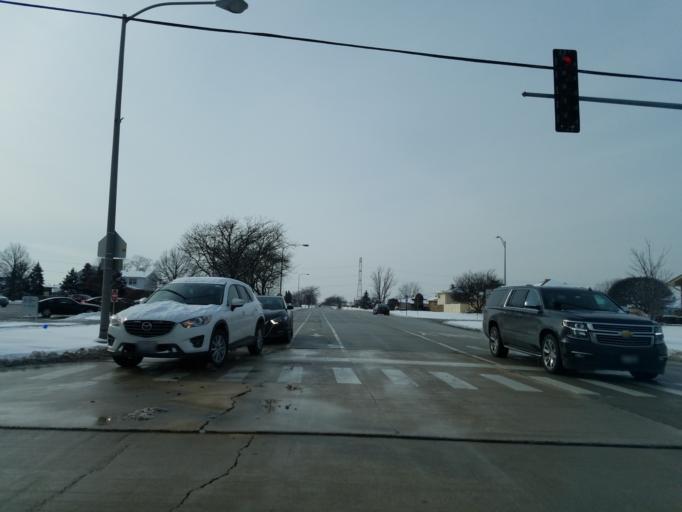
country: US
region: Illinois
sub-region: Cook County
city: Orland Hills
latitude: 41.5874
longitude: -87.8132
